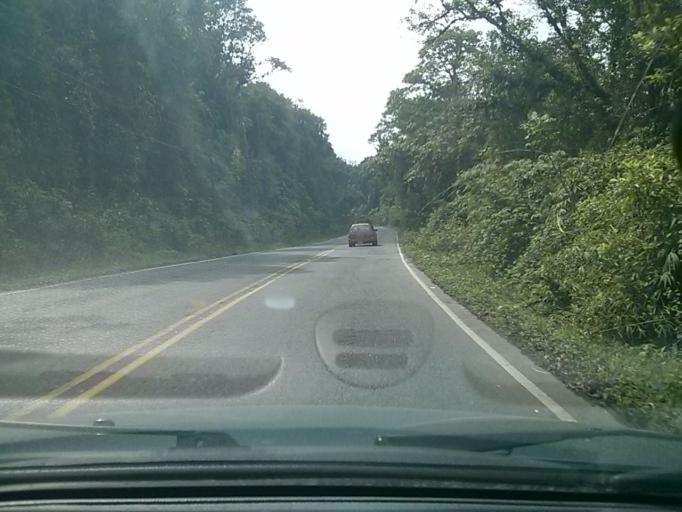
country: CR
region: Cartago
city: Tobosi
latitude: 9.7435
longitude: -83.9728
